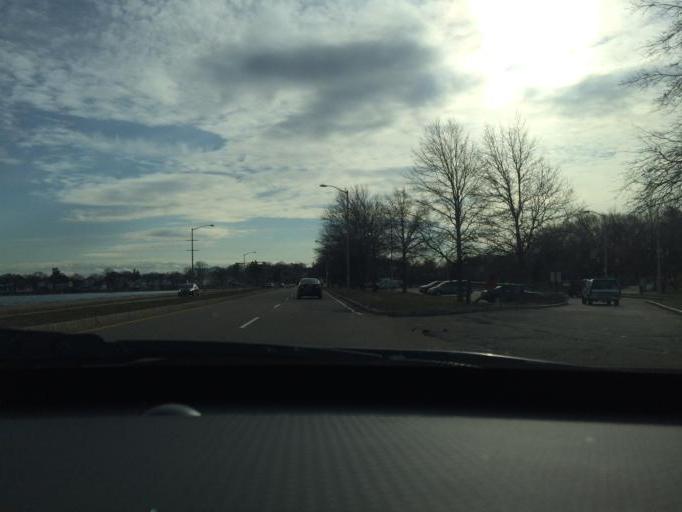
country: US
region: Massachusetts
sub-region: Norfolk County
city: Quincy
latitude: 42.2698
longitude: -70.9971
